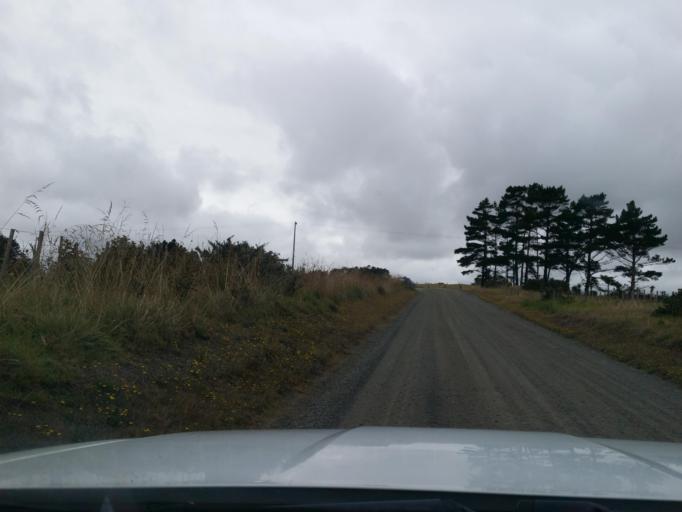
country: NZ
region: Northland
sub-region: Kaipara District
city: Dargaville
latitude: -36.0277
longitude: 173.8835
